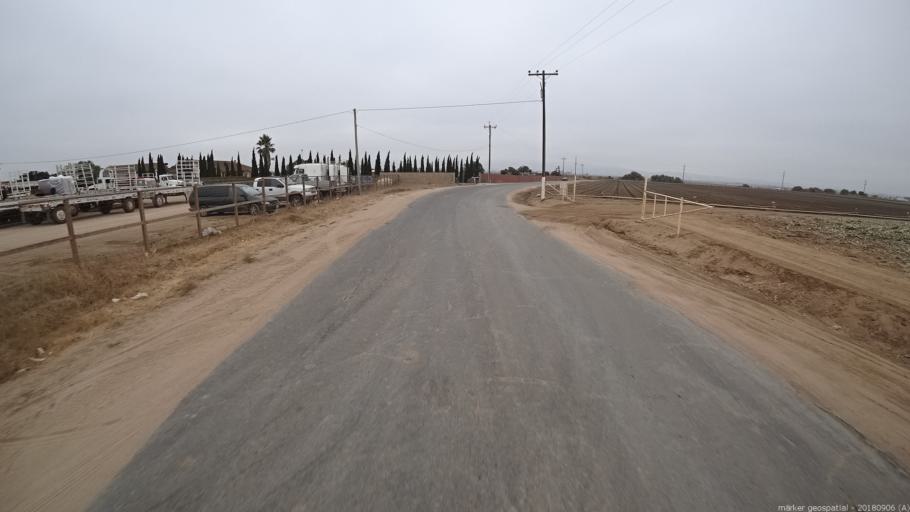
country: US
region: California
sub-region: Monterey County
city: Chualar
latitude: 36.6427
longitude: -121.5691
